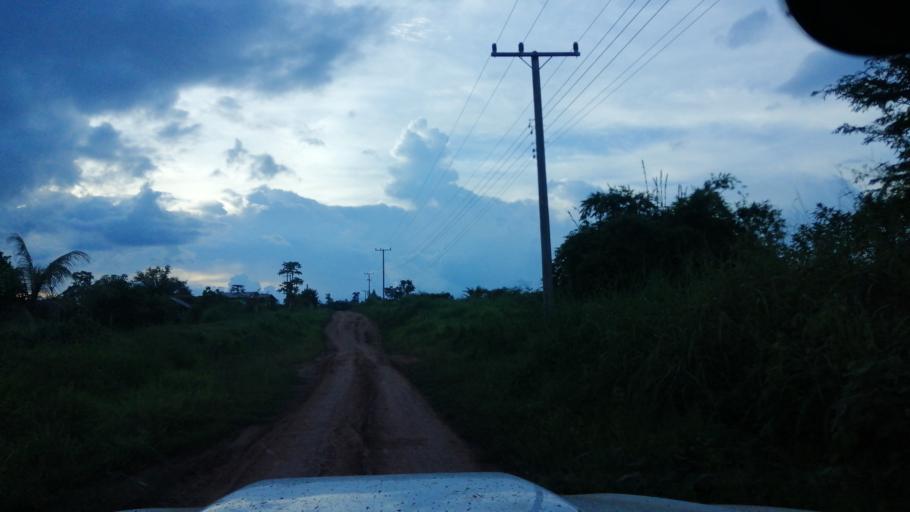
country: TH
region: Uttaradit
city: Ban Khok
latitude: 17.8751
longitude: 101.0812
